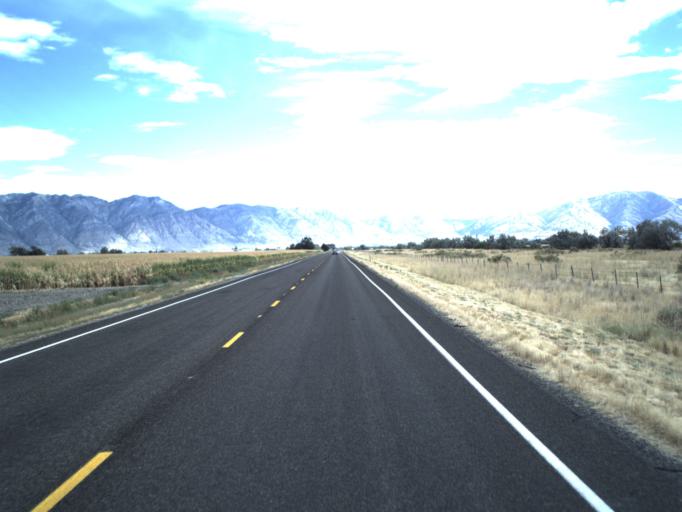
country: US
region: Utah
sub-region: Box Elder County
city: Elwood
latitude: 41.5683
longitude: -112.1933
